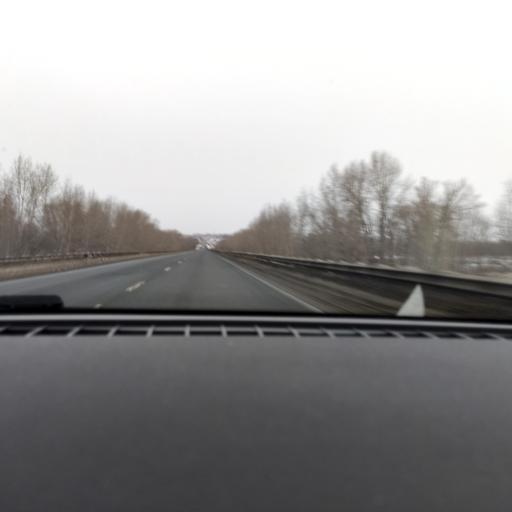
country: RU
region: Samara
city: Smyshlyayevka
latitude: 53.2220
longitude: 50.4985
